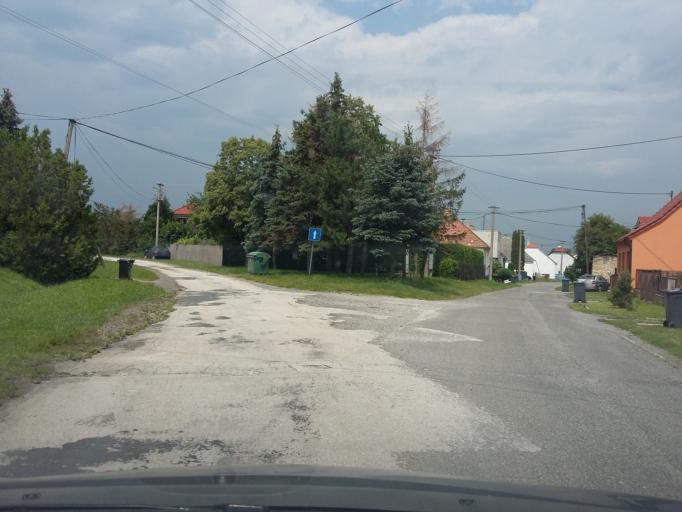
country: SK
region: Bratislavsky
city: Modra
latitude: 48.4657
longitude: 17.2276
